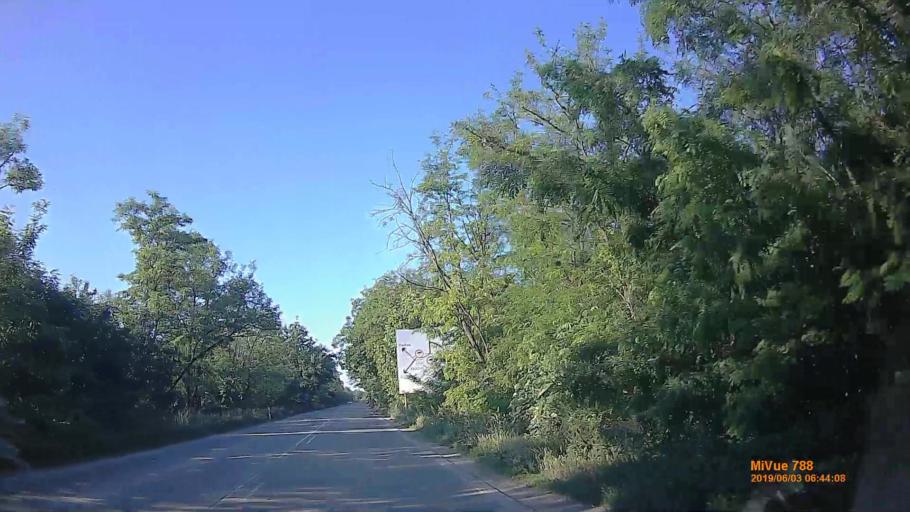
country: HU
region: Pest
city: Bugyi
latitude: 47.2474
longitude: 19.1291
